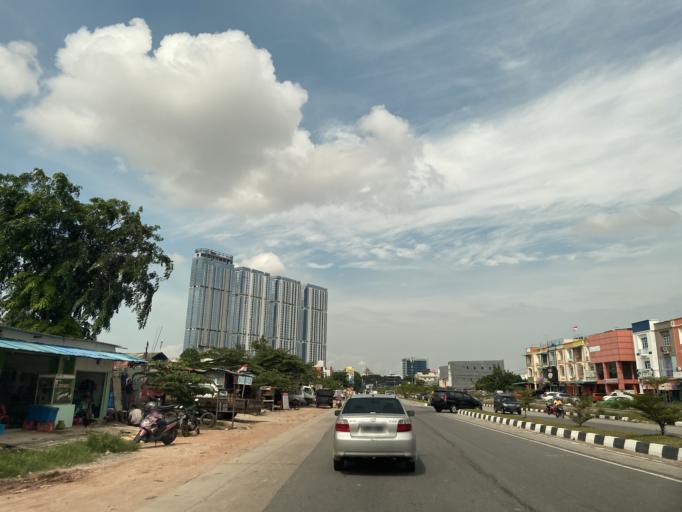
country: SG
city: Singapore
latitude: 1.1193
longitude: 104.0393
